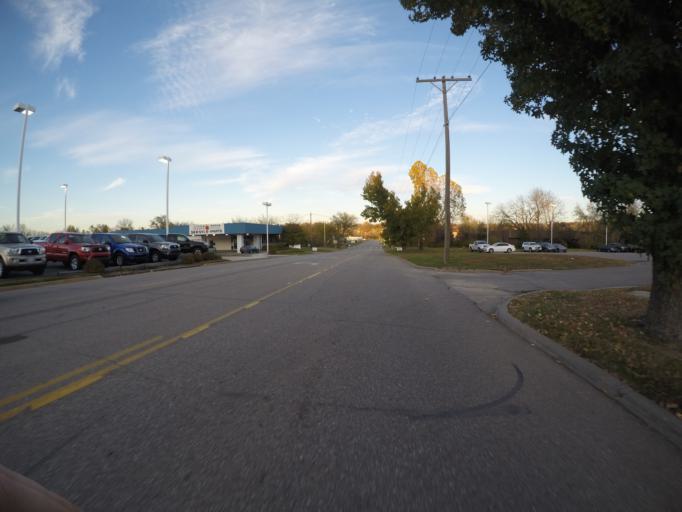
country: US
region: Kansas
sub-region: Riley County
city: Manhattan
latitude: 39.1811
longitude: -96.6083
